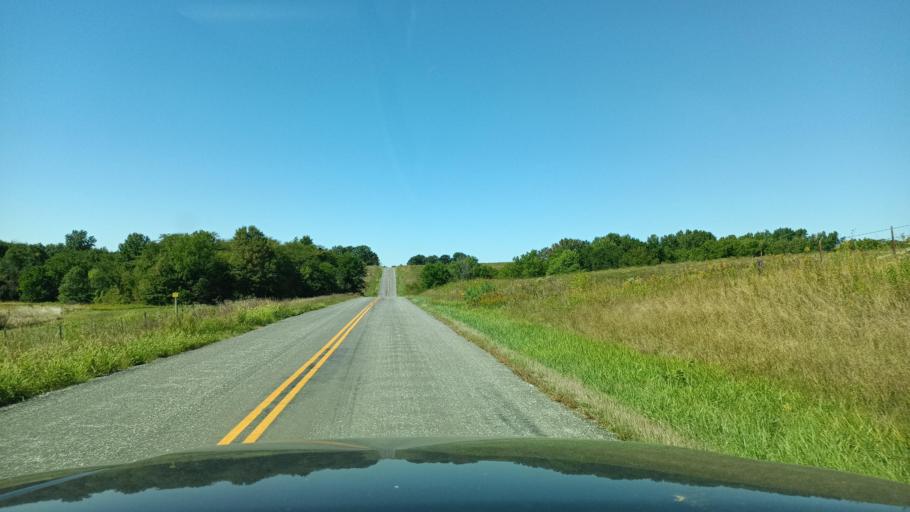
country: US
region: Missouri
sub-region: Adair County
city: Kirksville
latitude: 40.3302
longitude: -92.5329
